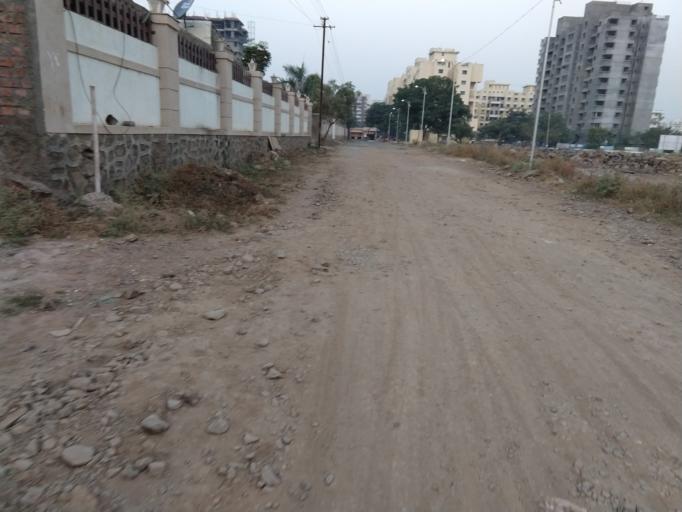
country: IN
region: Maharashtra
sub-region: Pune Division
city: Pune
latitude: 18.4388
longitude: 73.9110
